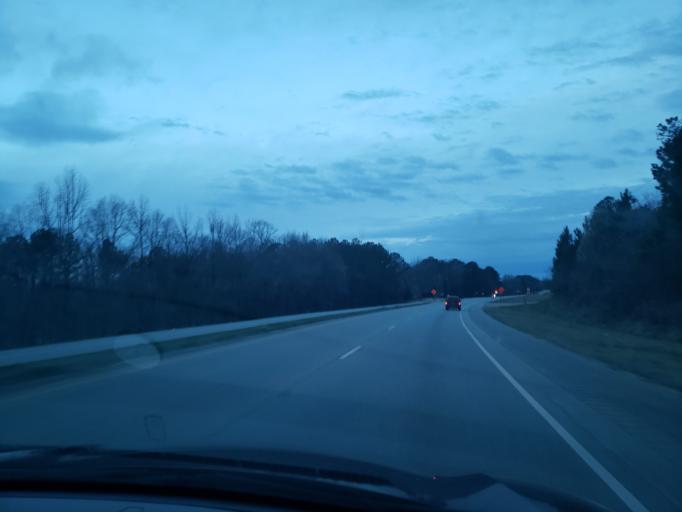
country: US
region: Alabama
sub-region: Lee County
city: Auburn
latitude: 32.6590
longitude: -85.4647
